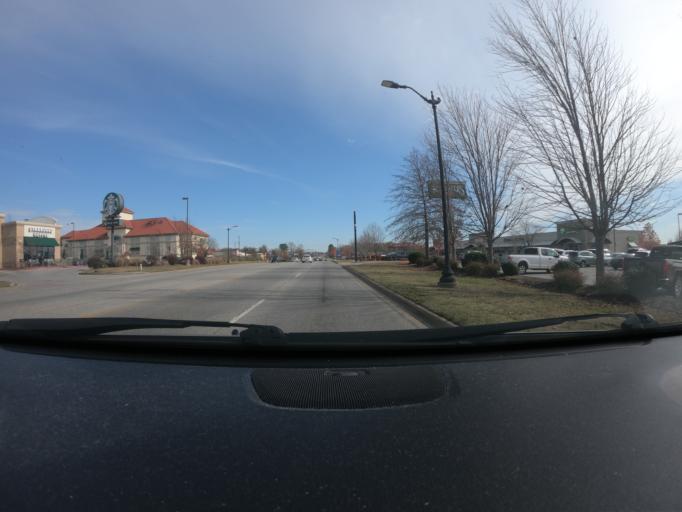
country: US
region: Arkansas
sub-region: Benton County
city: Bentonville
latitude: 36.3353
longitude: -94.2010
